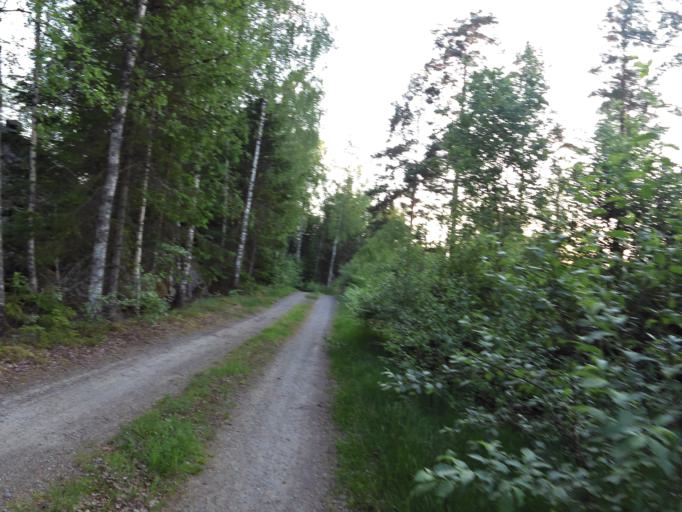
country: SE
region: Blekinge
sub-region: Olofstroms Kommun
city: Olofstroem
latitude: 56.4061
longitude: 14.5439
